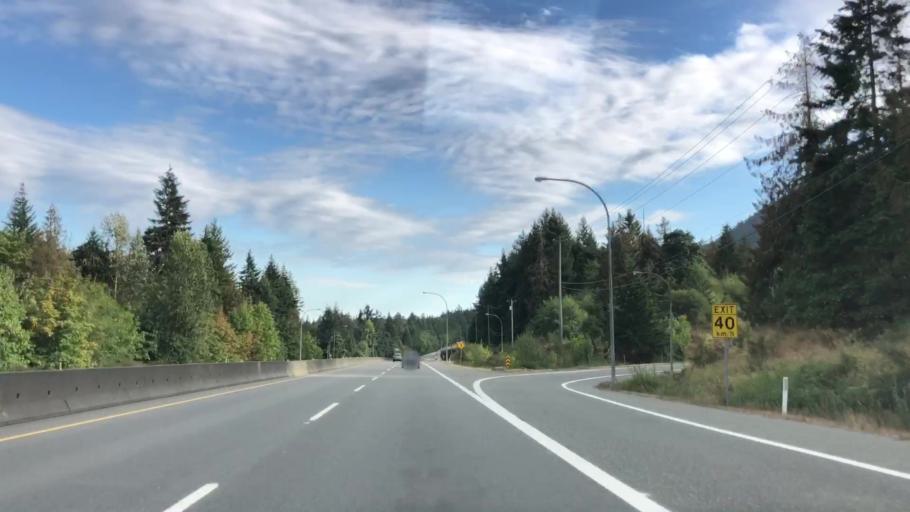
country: CA
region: British Columbia
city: North Saanich
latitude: 48.6152
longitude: -123.5416
